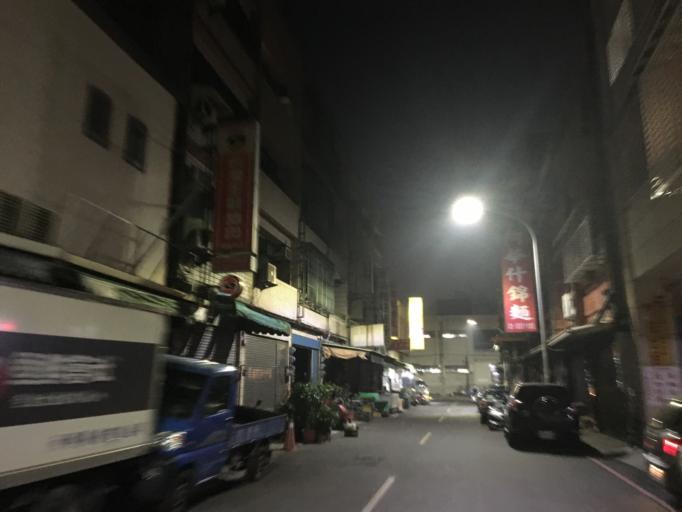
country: TW
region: Taiwan
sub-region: Hsinchu
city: Hsinchu
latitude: 24.8130
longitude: 120.9787
